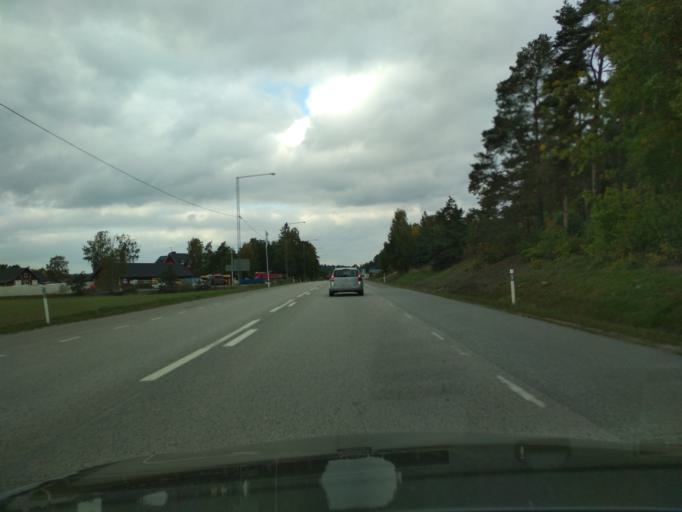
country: SE
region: Stockholm
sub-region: Vallentuna Kommun
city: Vallentuna
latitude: 59.5388
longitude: 18.0541
